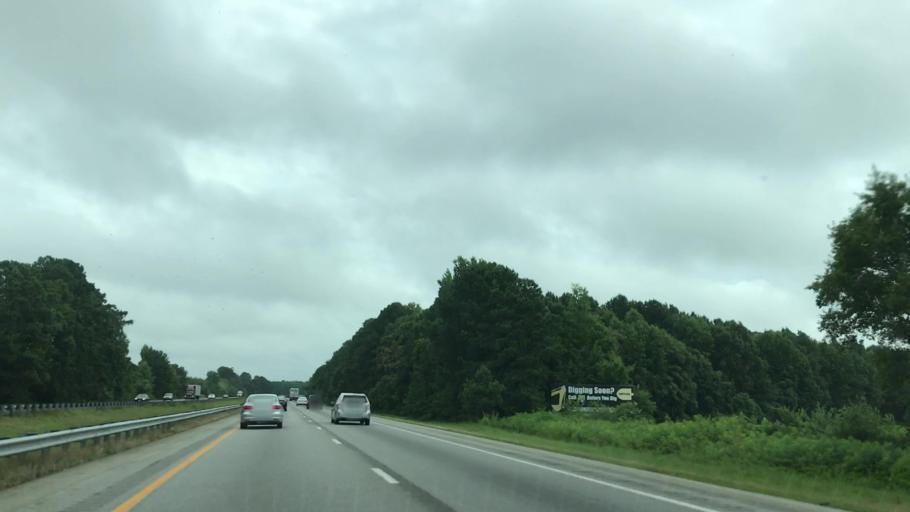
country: US
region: North Carolina
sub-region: Northampton County
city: Gaston
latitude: 36.4940
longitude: -77.5990
